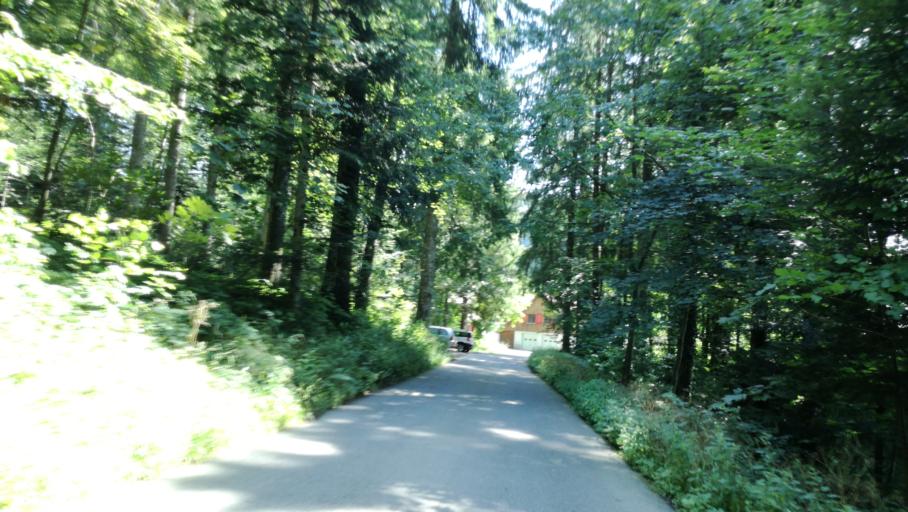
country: CH
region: Zug
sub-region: Zug
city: Unterageri
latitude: 47.1483
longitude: 8.5961
